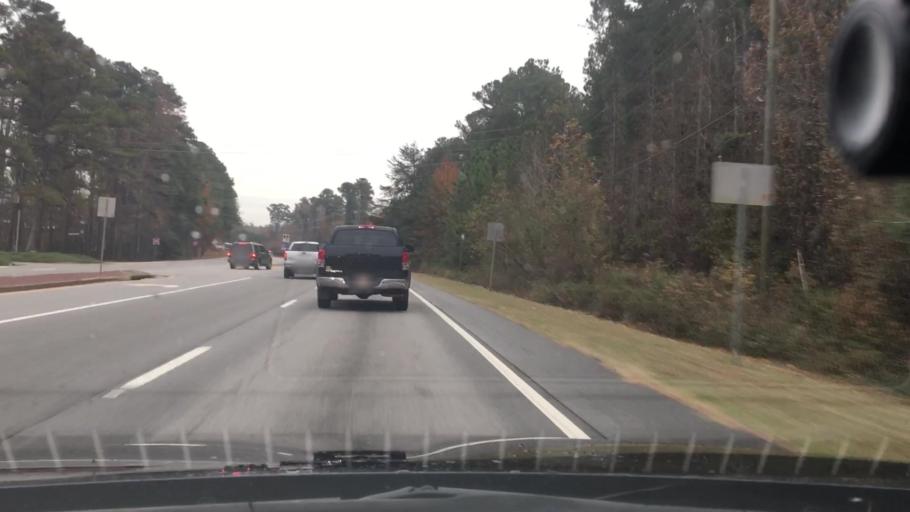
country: US
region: Georgia
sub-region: Fayette County
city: Peachtree City
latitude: 33.4025
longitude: -84.5981
